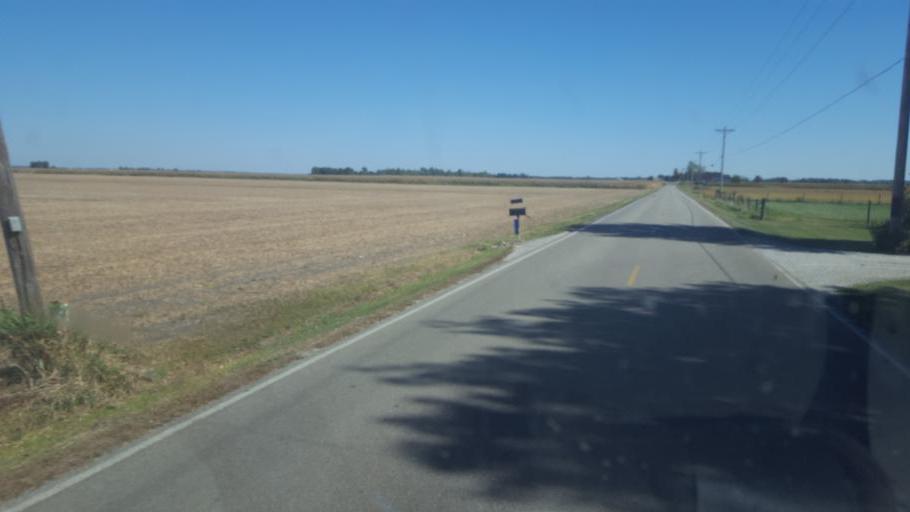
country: US
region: Ohio
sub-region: Huron County
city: Willard
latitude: 40.9820
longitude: -82.7707
